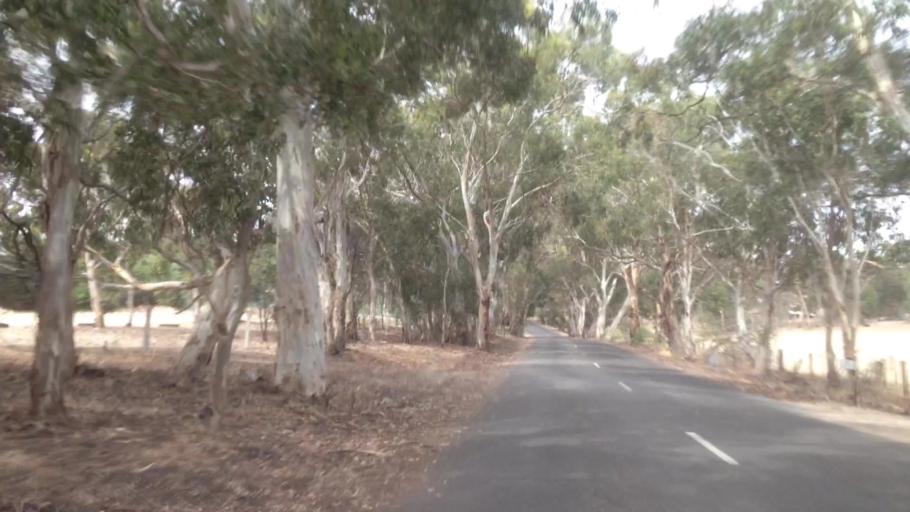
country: AU
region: South Australia
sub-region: Barossa
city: Williamstown
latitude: -34.6431
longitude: 138.8518
